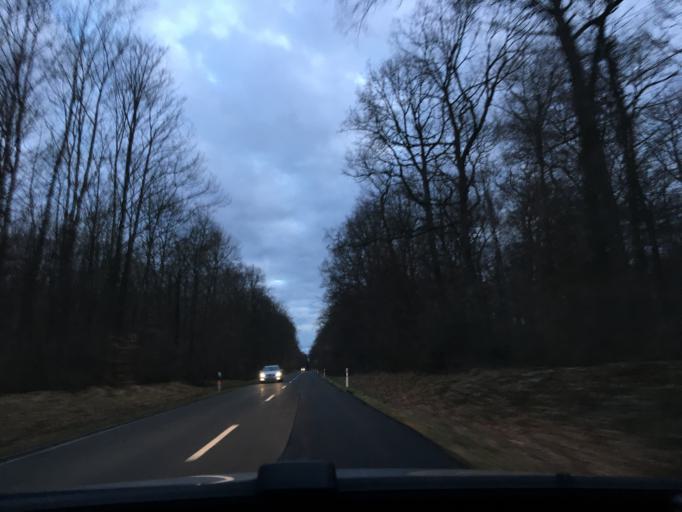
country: DE
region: Rheinland-Pfalz
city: Bechenheim
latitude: 49.7180
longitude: 8.0021
